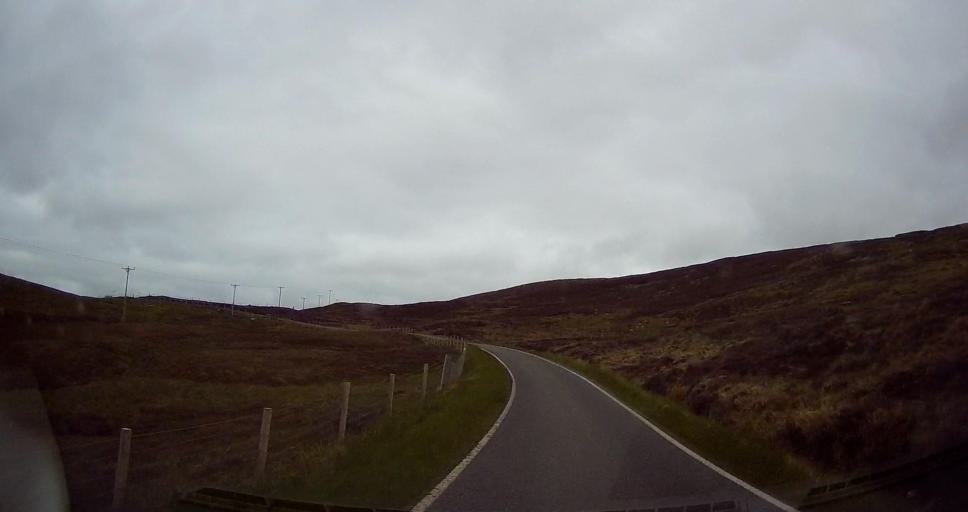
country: GB
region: Scotland
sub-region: Shetland Islands
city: Lerwick
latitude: 60.3085
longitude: -1.3380
